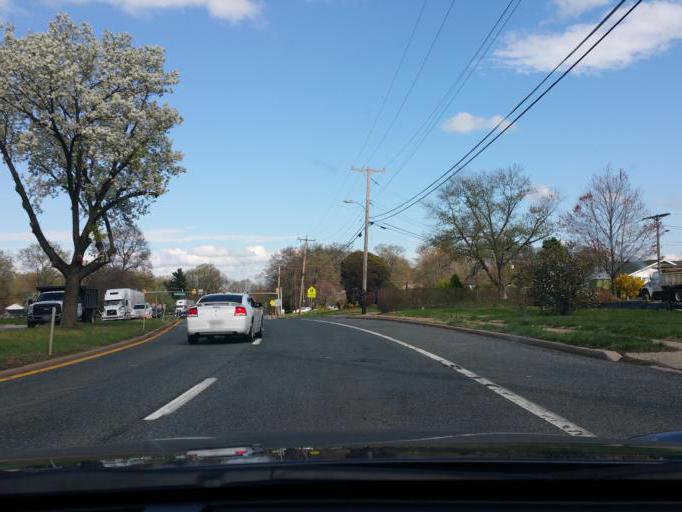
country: US
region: Maryland
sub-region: Harford County
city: Aberdeen
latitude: 39.5223
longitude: -76.1732
